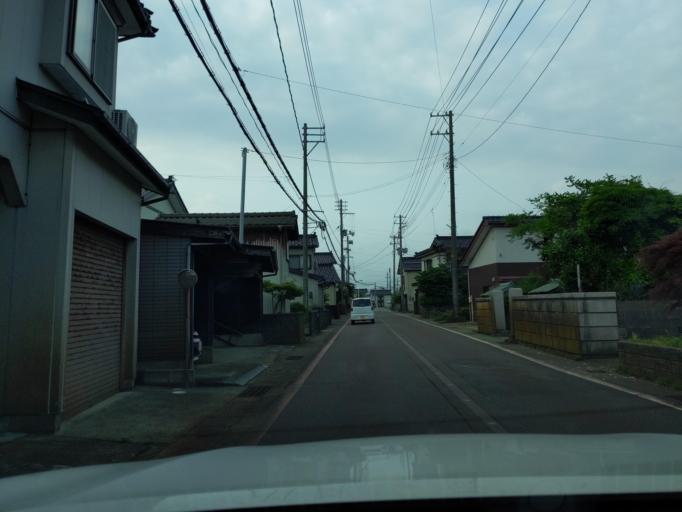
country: JP
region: Niigata
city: Kashiwazaki
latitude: 37.3871
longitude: 138.5784
